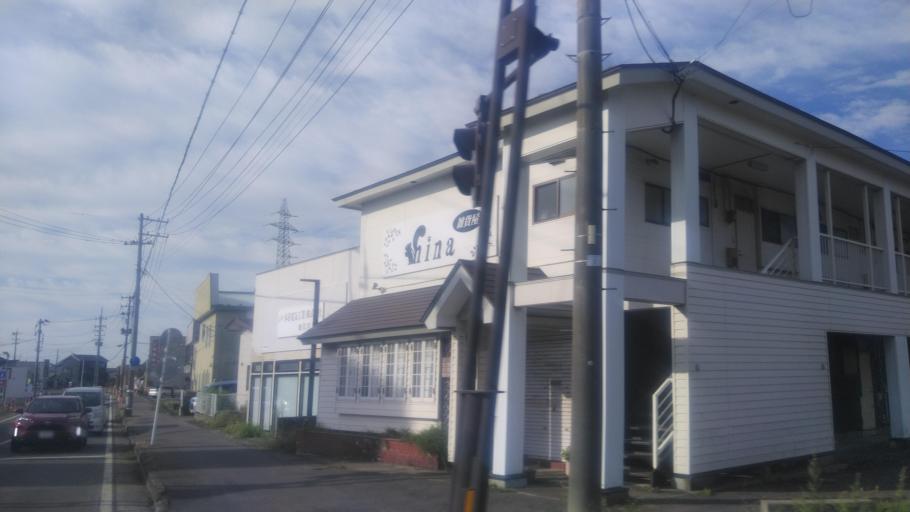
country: JP
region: Akita
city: Noshiromachi
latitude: 40.1902
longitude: 140.0374
